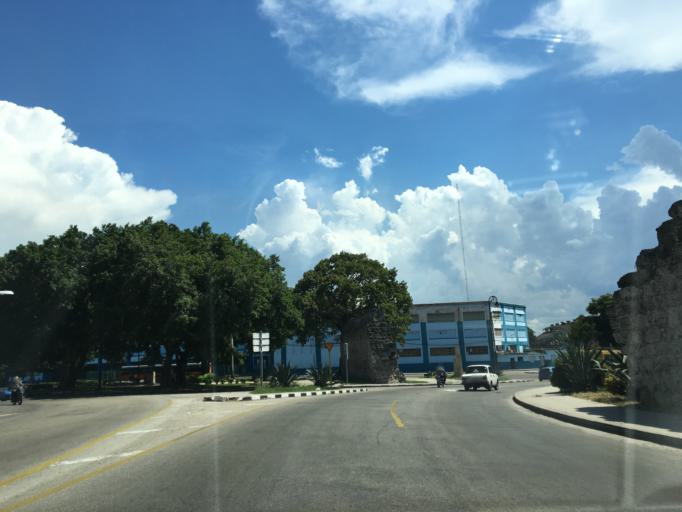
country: CU
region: La Habana
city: La Habana Vieja
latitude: 23.1289
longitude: -82.3531
